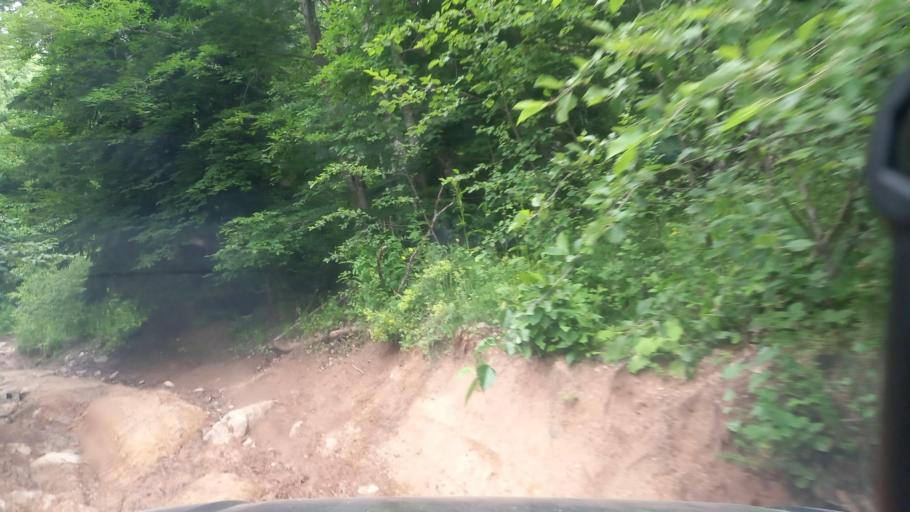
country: RU
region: Karachayevo-Cherkesiya
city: Kurdzhinovo
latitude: 43.8099
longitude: 40.8653
